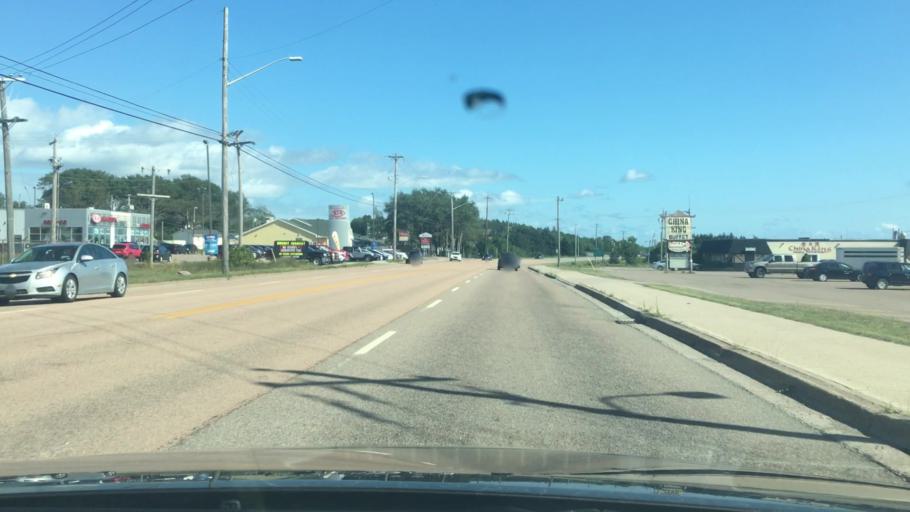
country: CA
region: Nova Scotia
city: Port Hawkesbury
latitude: 45.6139
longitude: -61.3493
